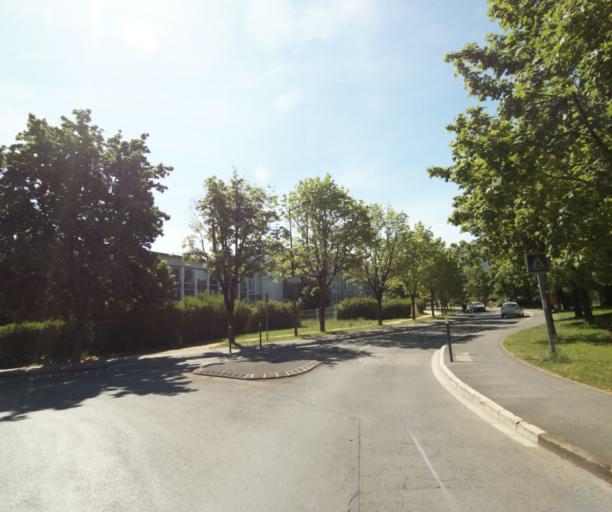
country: FR
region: Champagne-Ardenne
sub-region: Departement des Ardennes
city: Charleville-Mezieres
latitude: 49.7488
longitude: 4.7204
